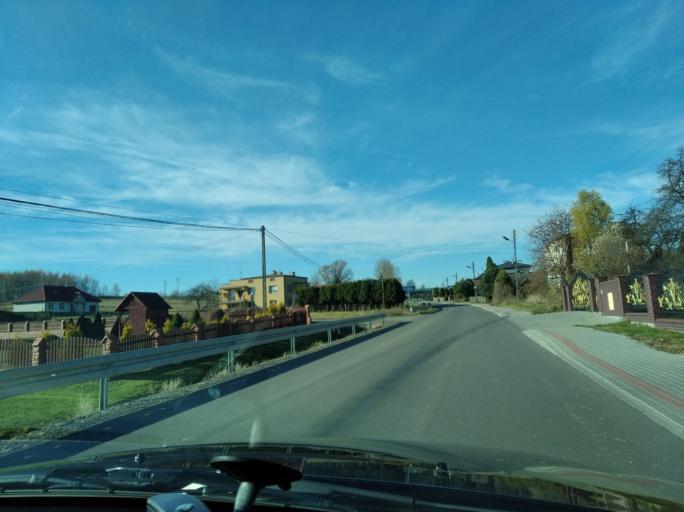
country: PL
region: Subcarpathian Voivodeship
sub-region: Powiat rzeszowski
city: Kielanowka
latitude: 50.0105
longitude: 21.9269
